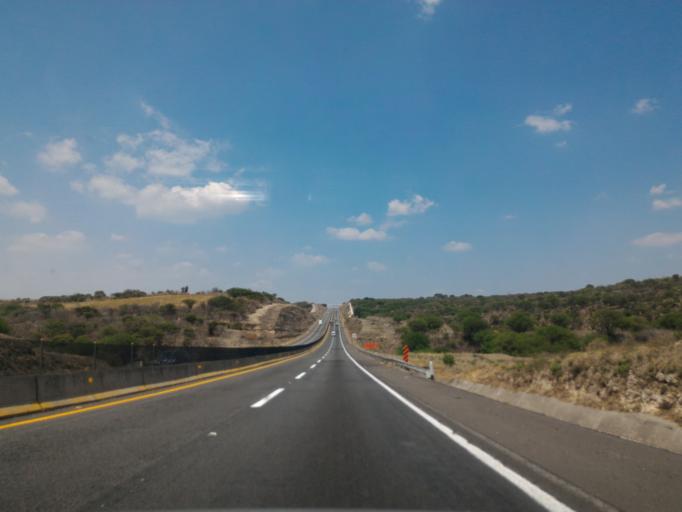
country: MX
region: Jalisco
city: Jalostotitlan
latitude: 21.1707
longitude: -102.3960
